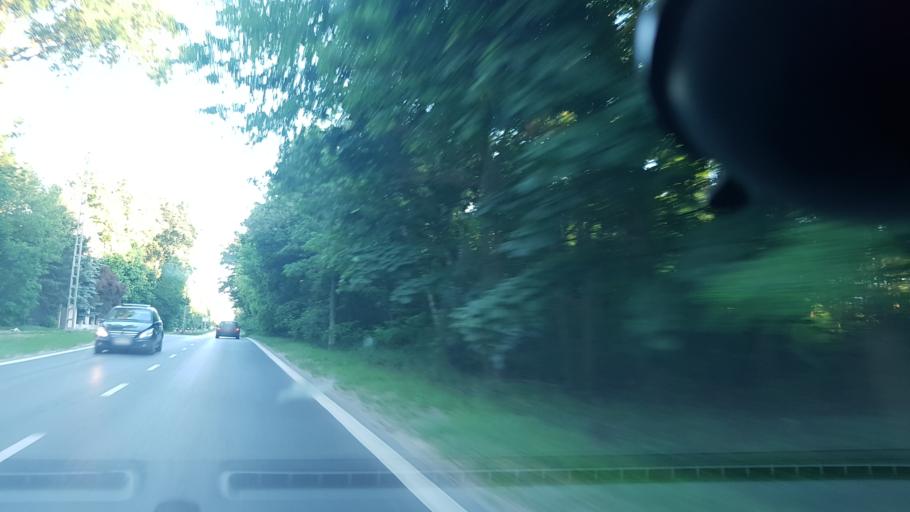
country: PL
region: Masovian Voivodeship
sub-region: Warszawa
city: Wawer
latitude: 52.1786
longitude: 21.1949
